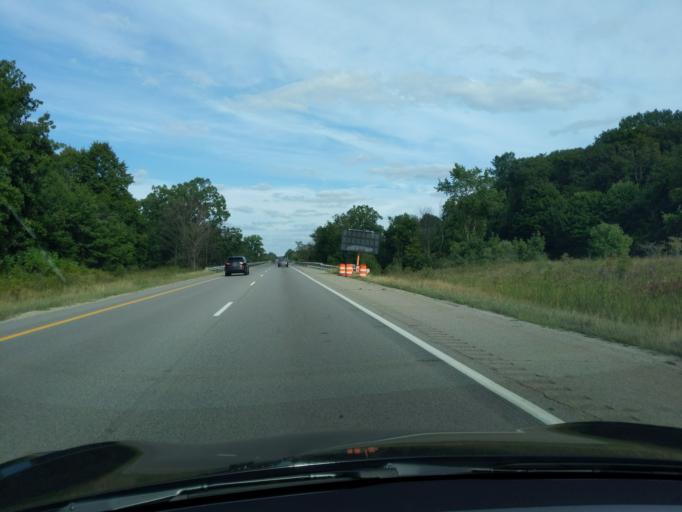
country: US
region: Michigan
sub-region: Ottawa County
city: Coopersville
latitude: 43.0699
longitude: -86.0187
